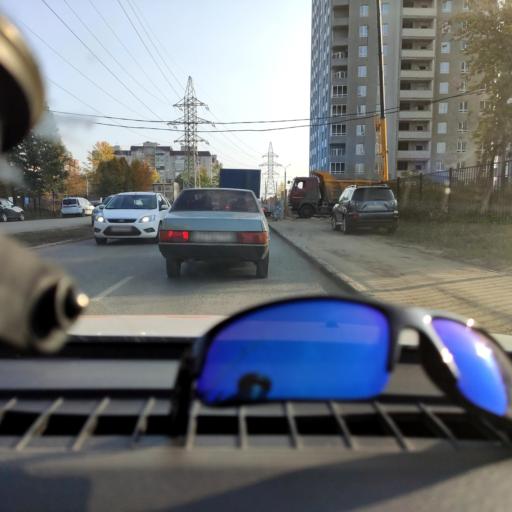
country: RU
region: Samara
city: Samara
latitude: 53.2136
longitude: 50.2026
